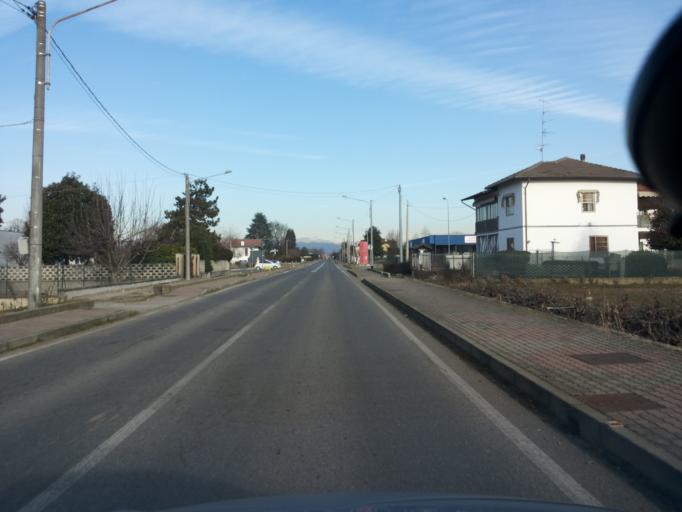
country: IT
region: Piedmont
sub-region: Provincia di Vercelli
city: Ghislarengo
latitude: 45.5336
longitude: 8.3857
